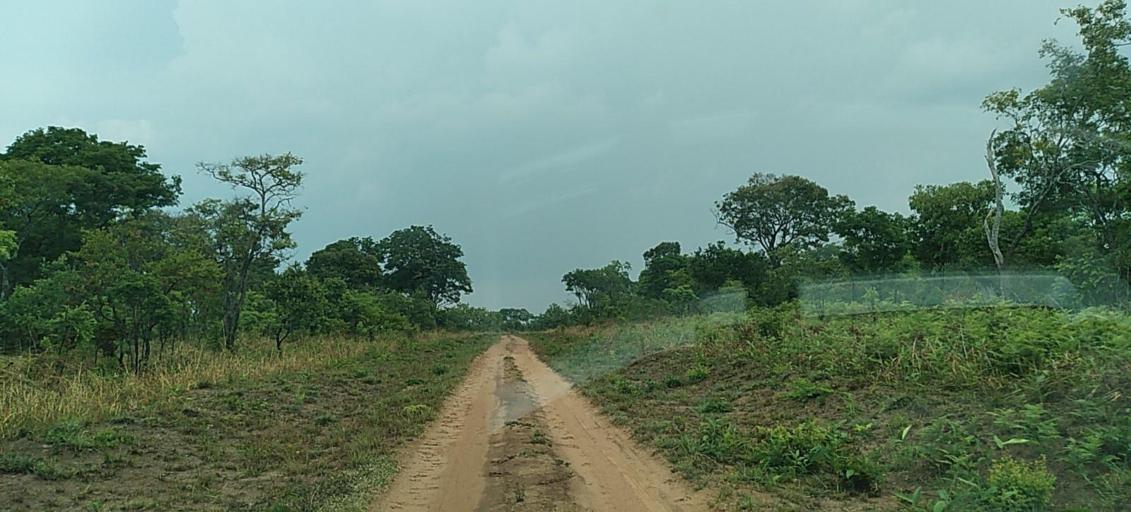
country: ZM
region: North-Western
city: Mwinilunga
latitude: -11.4393
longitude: 24.5936
